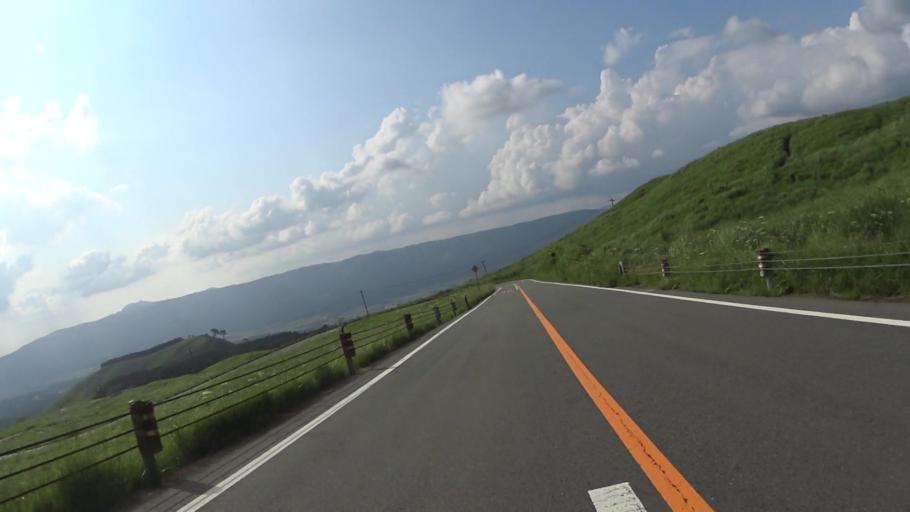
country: JP
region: Kumamoto
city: Aso
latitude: 32.9037
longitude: 131.0372
